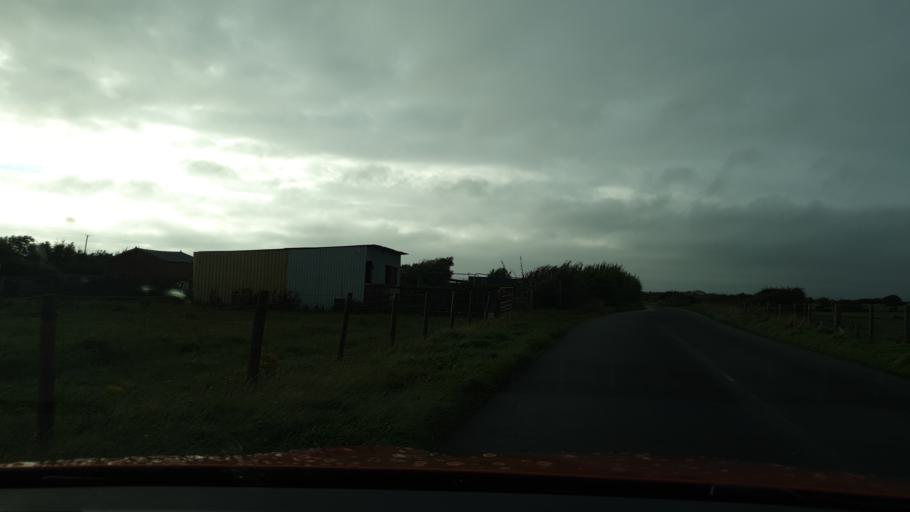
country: GB
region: England
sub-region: Cumbria
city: Barrow in Furness
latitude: 54.0794
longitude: -3.2316
